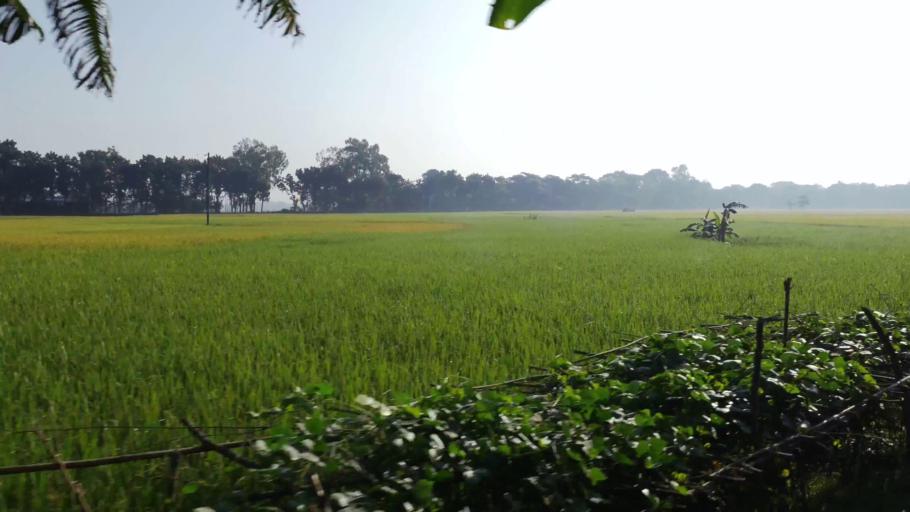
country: BD
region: Dhaka
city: Jamalpur
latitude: 24.8632
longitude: 90.0685
